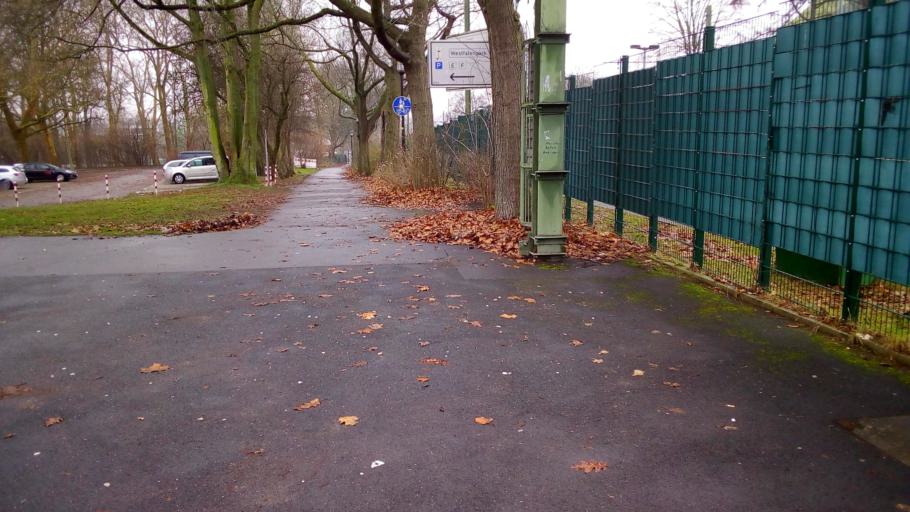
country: DE
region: North Rhine-Westphalia
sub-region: Regierungsbezirk Arnsberg
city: Dortmund
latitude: 51.4941
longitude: 7.4579
